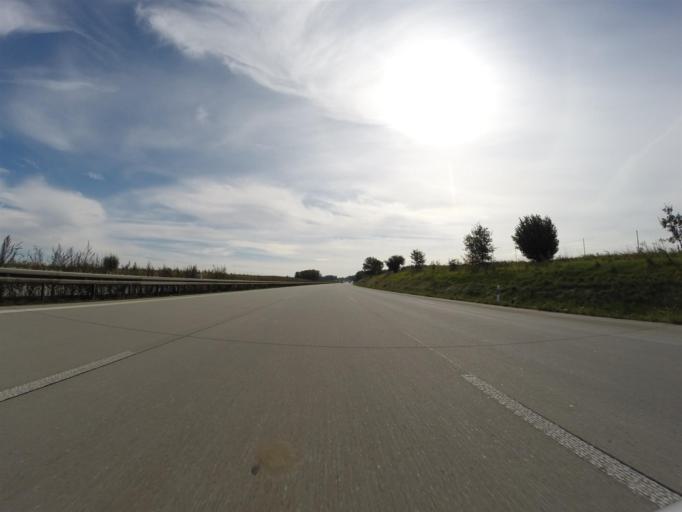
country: DE
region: Saxony
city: Remse
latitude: 50.8394
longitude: 12.5896
